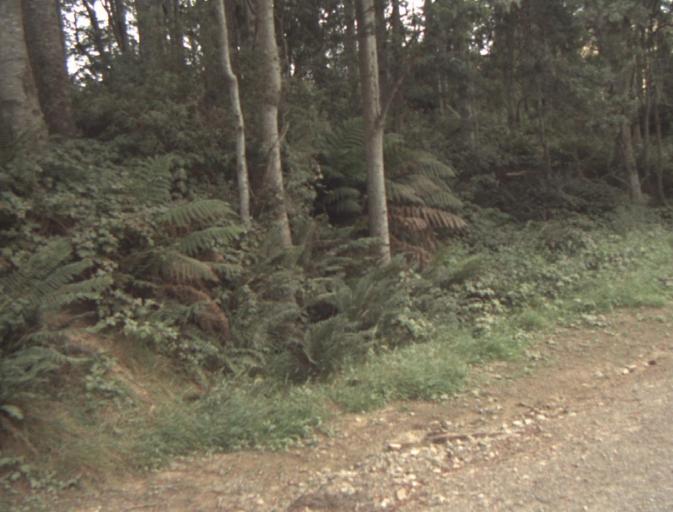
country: AU
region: Tasmania
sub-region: Dorset
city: Scottsdale
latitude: -41.3425
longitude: 147.4338
